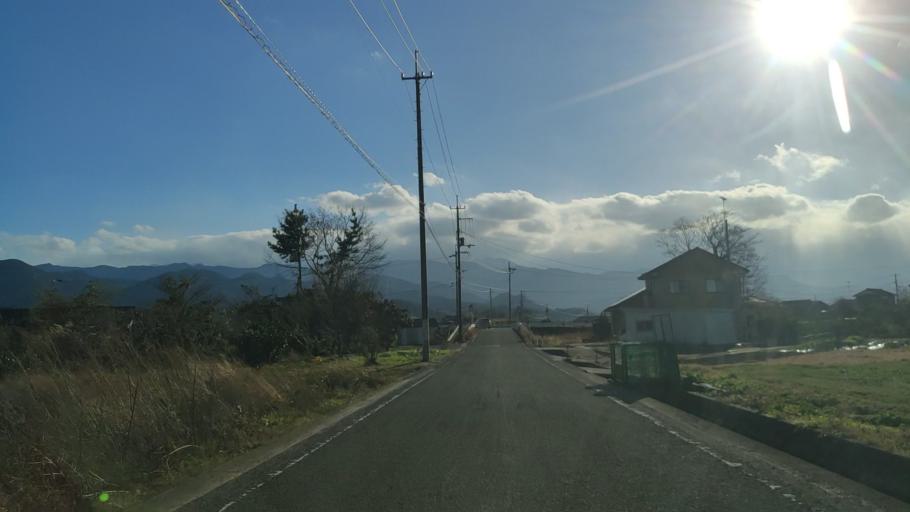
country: JP
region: Ehime
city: Saijo
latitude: 33.9094
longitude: 133.0971
